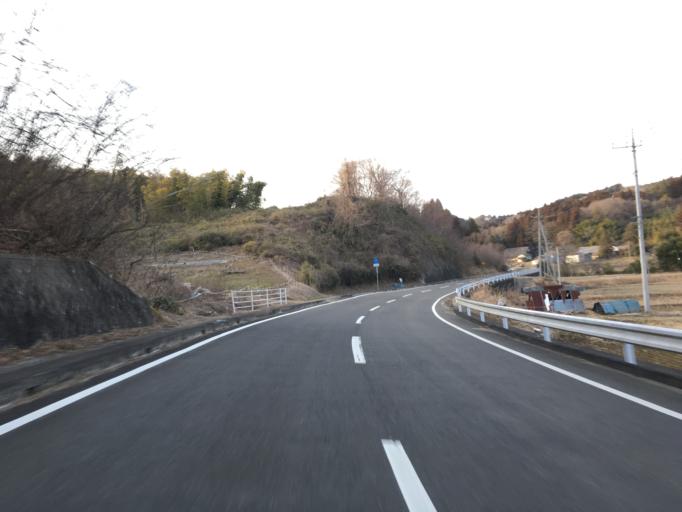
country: JP
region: Ibaraki
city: Daigo
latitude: 36.7925
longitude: 140.4118
